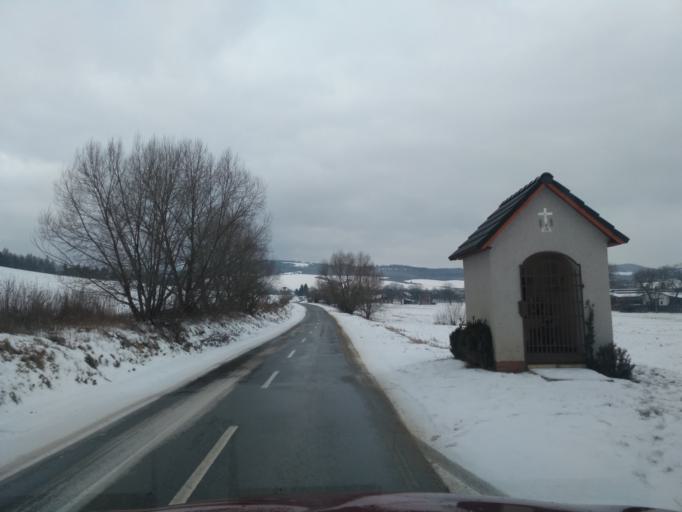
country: SK
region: Presovsky
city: Sabinov
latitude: 49.0534
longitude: 21.0764
